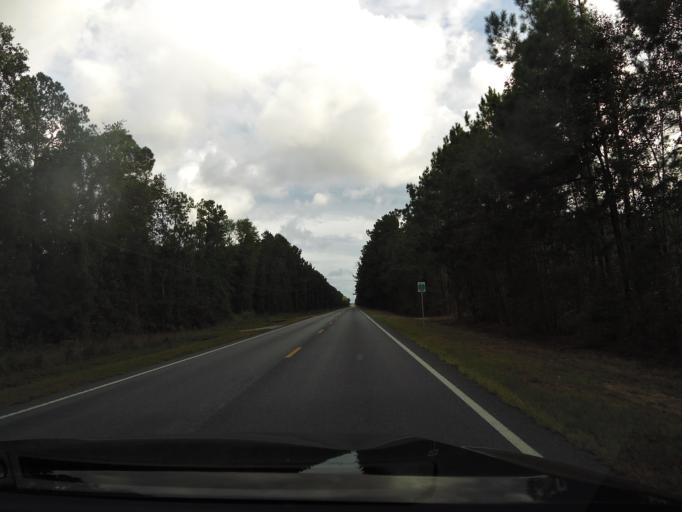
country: US
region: Georgia
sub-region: Liberty County
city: Midway
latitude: 31.6791
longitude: -81.4047
